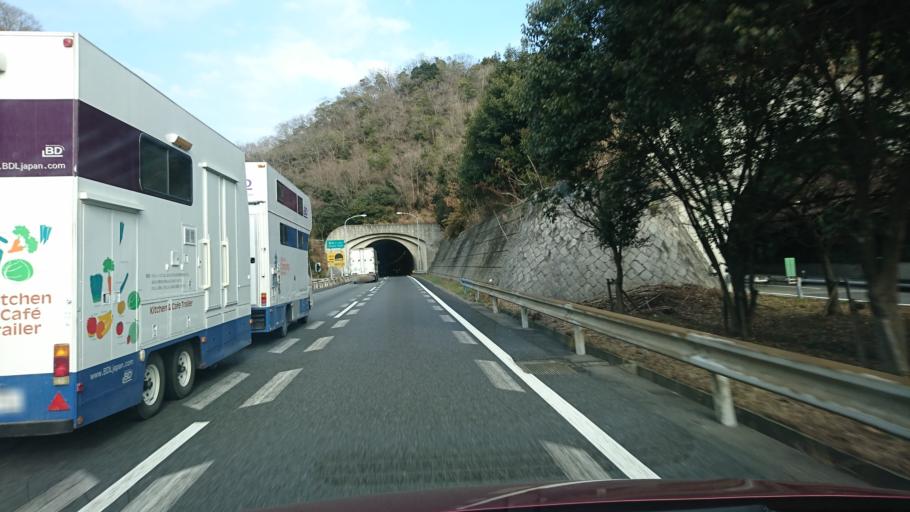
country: JP
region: Hyogo
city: Kariya
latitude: 34.7882
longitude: 134.2152
